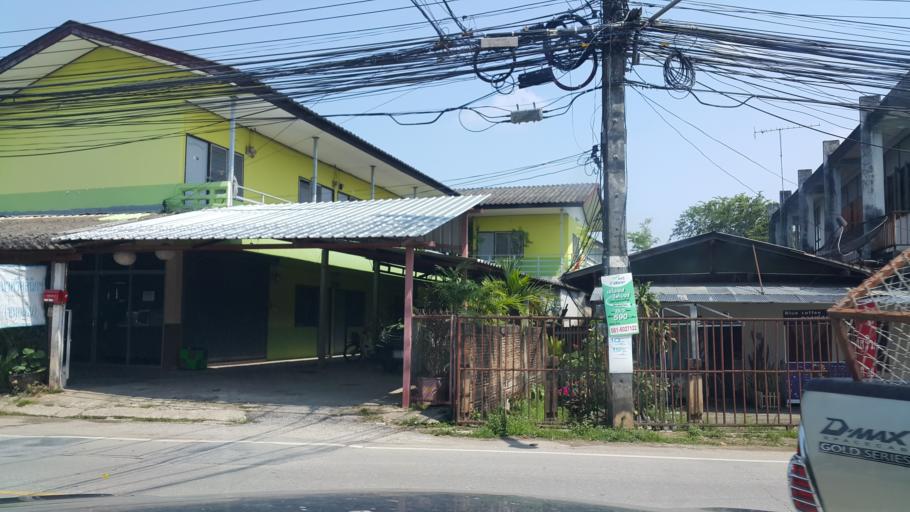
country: TH
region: Chiang Rai
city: Chiang Rai
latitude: 19.9288
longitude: 99.8474
